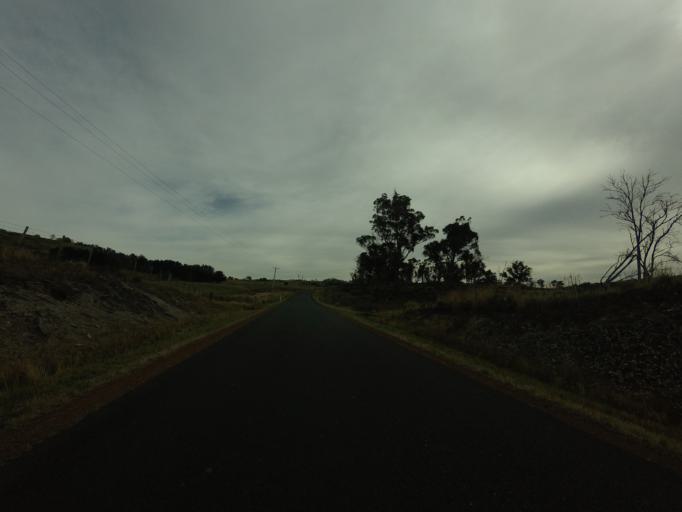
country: AU
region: Tasmania
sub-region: Sorell
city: Sorell
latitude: -42.4595
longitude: 147.5731
